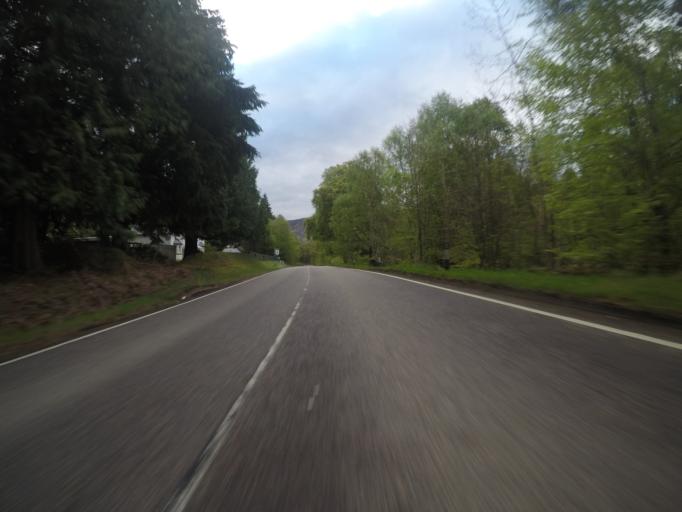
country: GB
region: Scotland
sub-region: Highland
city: Spean Bridge
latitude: 57.0720
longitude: -4.7784
